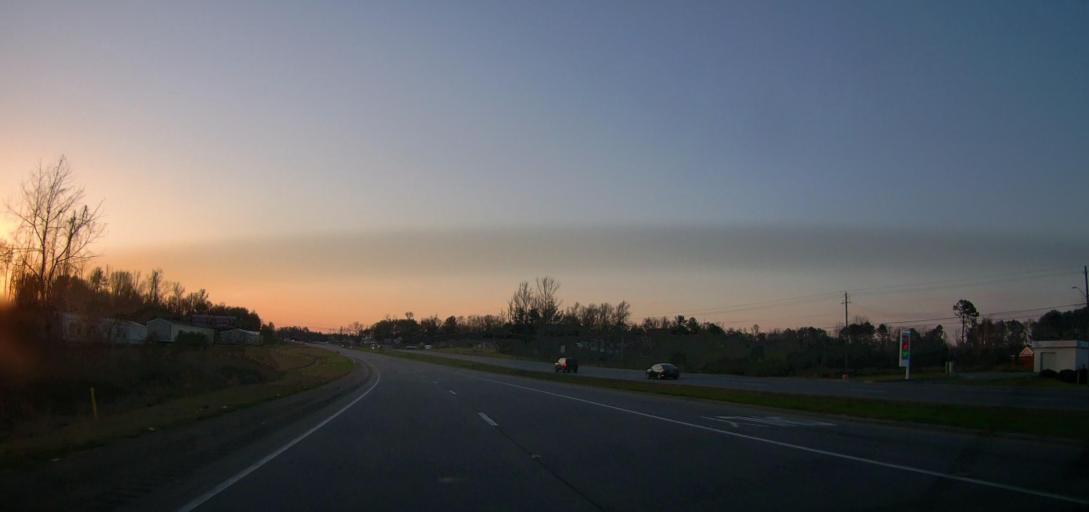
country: US
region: Alabama
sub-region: Tallapoosa County
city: Alexander City
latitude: 32.9678
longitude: -86.0102
